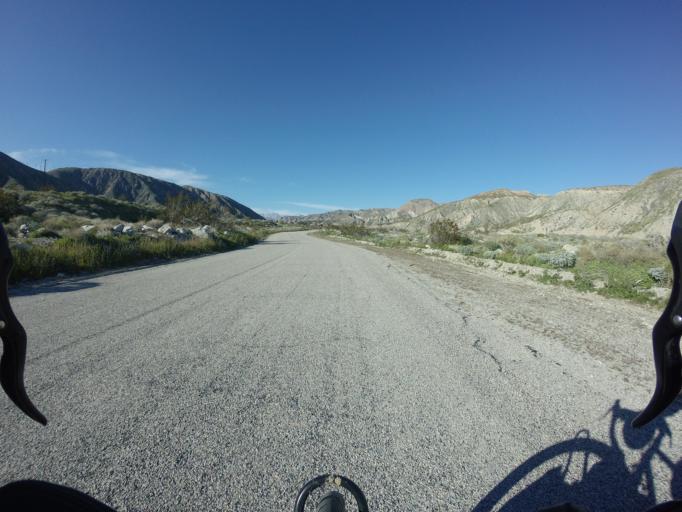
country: US
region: California
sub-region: Riverside County
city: Garnet
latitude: 33.9406
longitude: -116.6415
